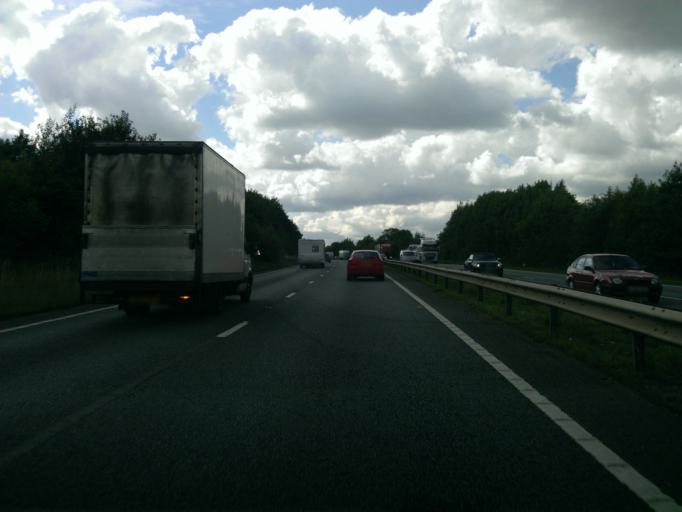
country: GB
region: England
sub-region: Leicestershire
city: Market Harborough
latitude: 52.4066
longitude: -0.9490
